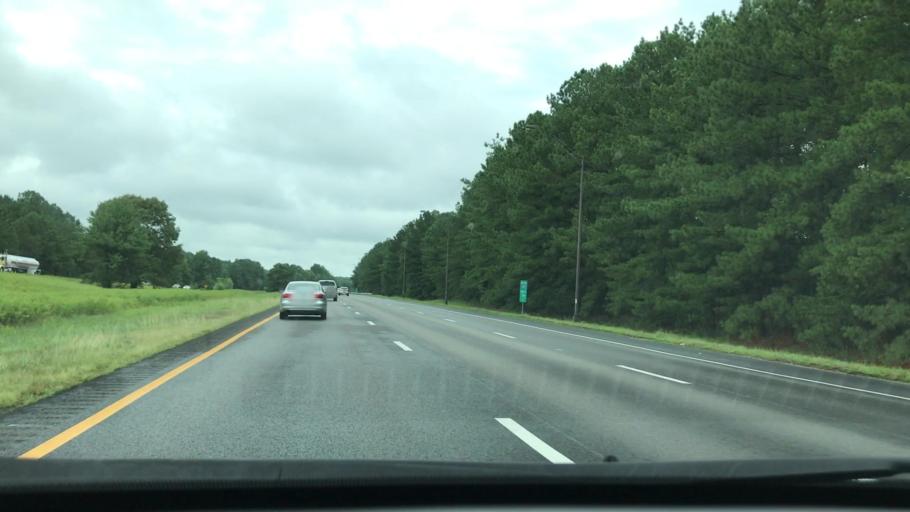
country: US
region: Virginia
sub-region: Sussex County
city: Sussex
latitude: 37.0197
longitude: -77.3918
